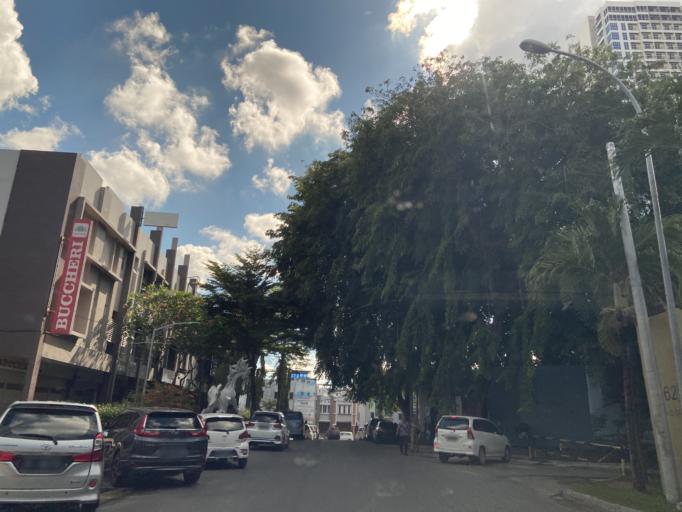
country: SG
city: Singapore
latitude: 1.1439
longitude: 104.0082
